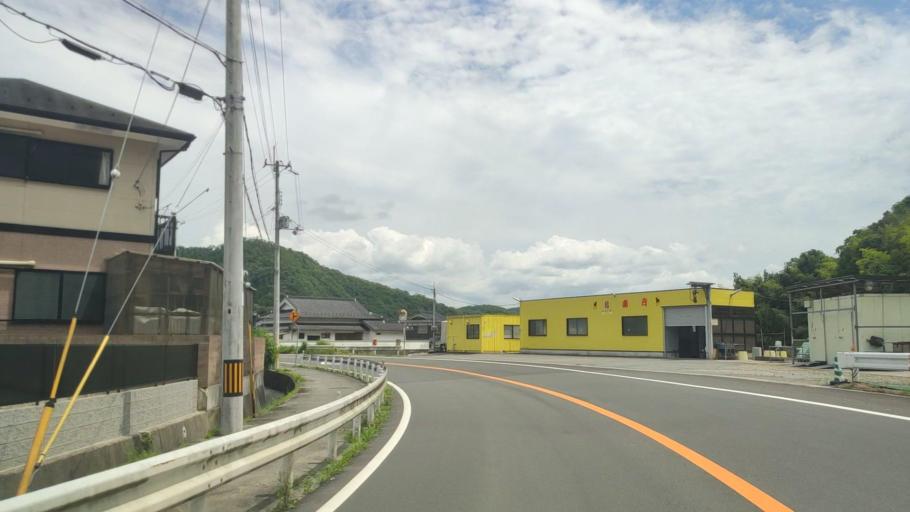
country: JP
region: Hyogo
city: Yamazakicho-nakabirose
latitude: 35.0300
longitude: 134.3662
